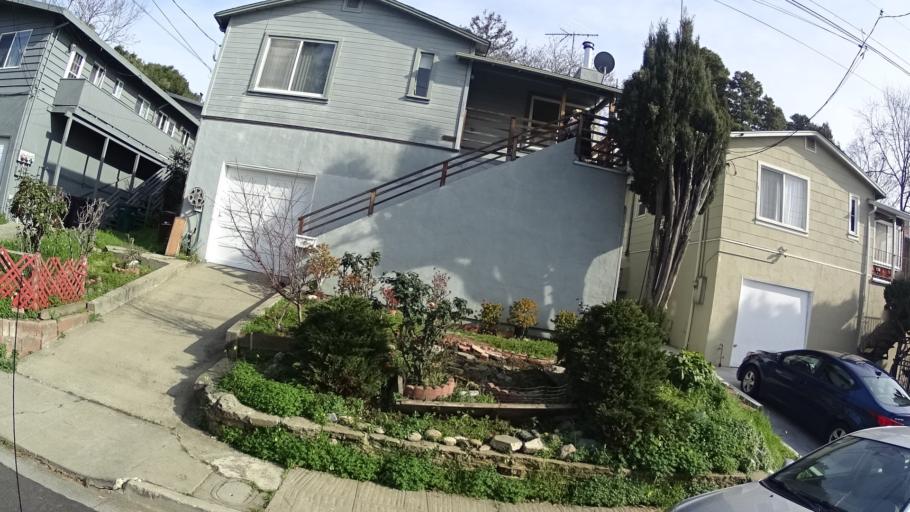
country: US
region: California
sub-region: Alameda County
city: Hayward
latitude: 37.6650
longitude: -122.0757
